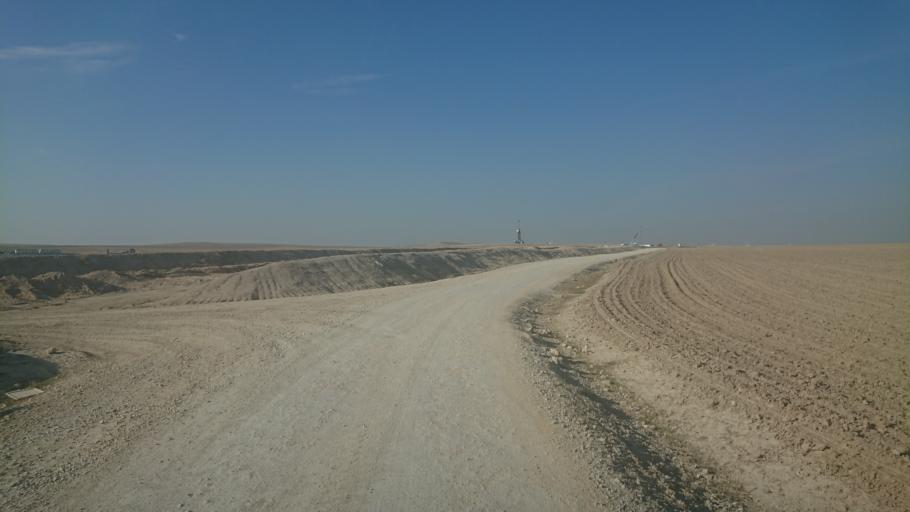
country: TR
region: Aksaray
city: Sultanhani
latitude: 38.0686
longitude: 33.6152
